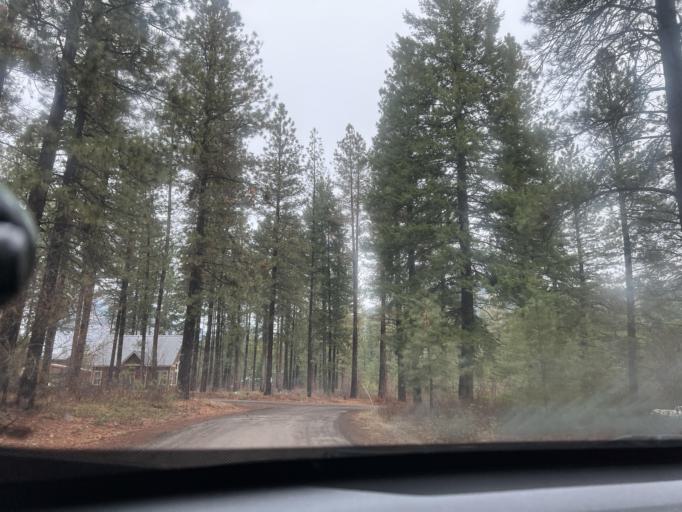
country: US
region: Washington
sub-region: Chelan County
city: Granite Falls
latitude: 48.5585
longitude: -120.3672
